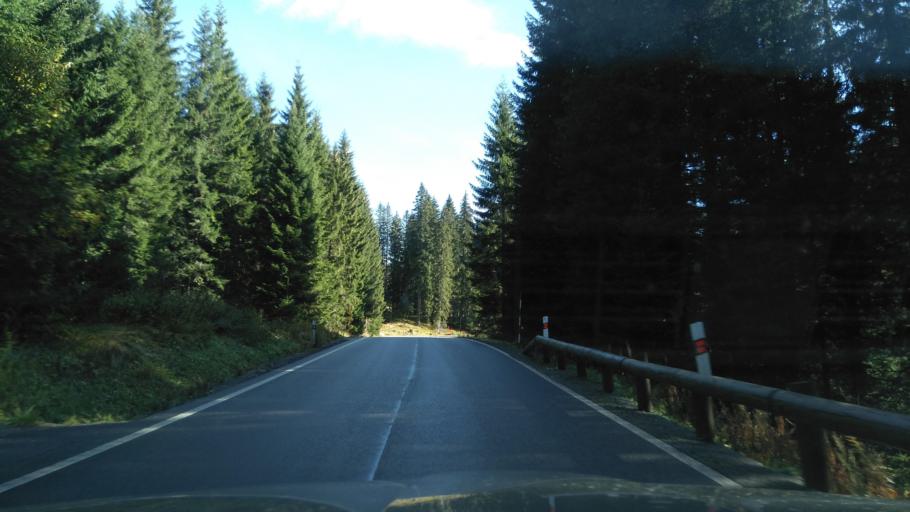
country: CZ
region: Plzensky
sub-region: Okres Klatovy
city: Kasperske Hory
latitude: 49.0232
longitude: 13.5053
